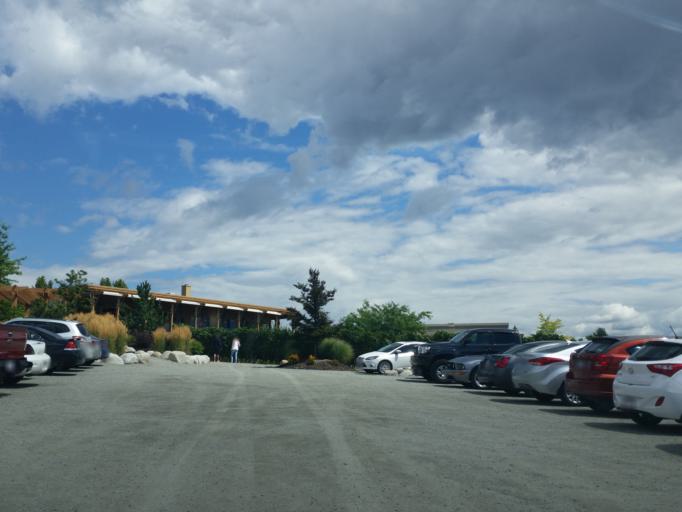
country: CA
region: British Columbia
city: West Kelowna
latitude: 49.8421
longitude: -119.5676
